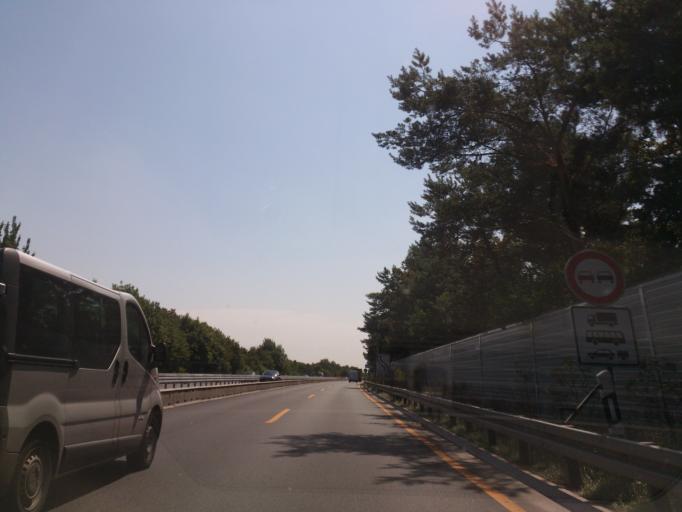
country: DE
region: North Rhine-Westphalia
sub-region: Regierungsbezirk Detmold
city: Hovelhof
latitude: 51.7916
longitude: 8.7030
